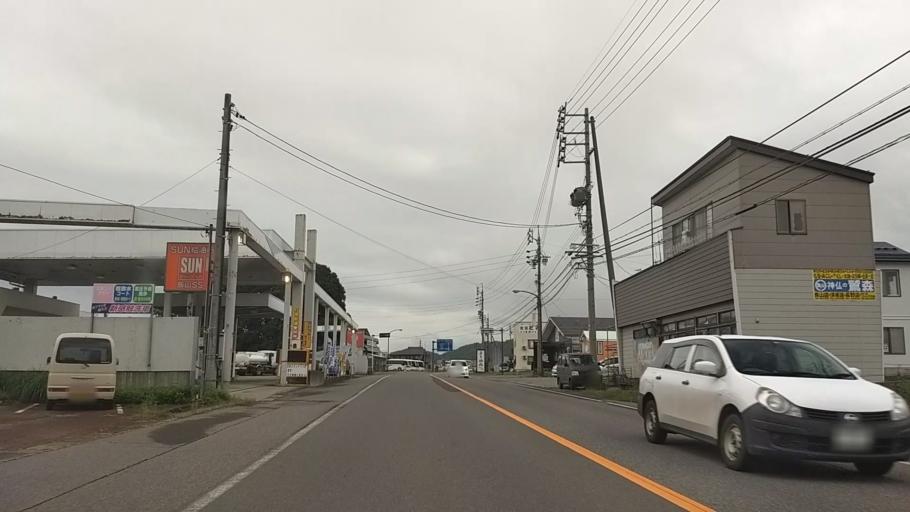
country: JP
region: Nagano
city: Iiyama
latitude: 36.8284
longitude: 138.3543
